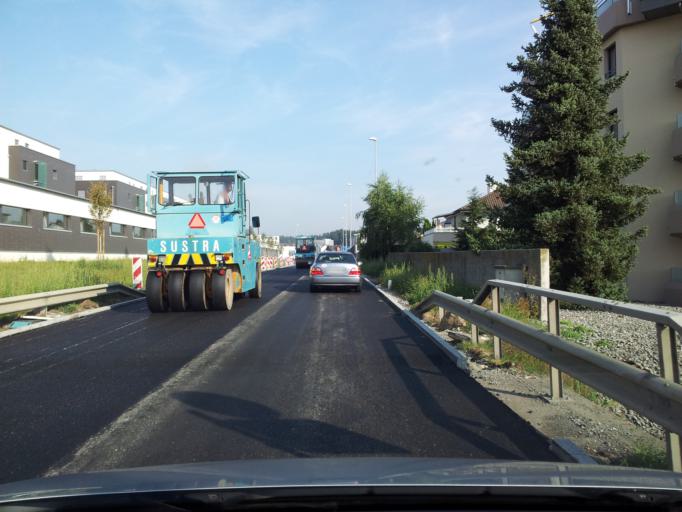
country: CH
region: Lucerne
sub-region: Sursee District
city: Sursee
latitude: 47.1684
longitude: 8.0981
